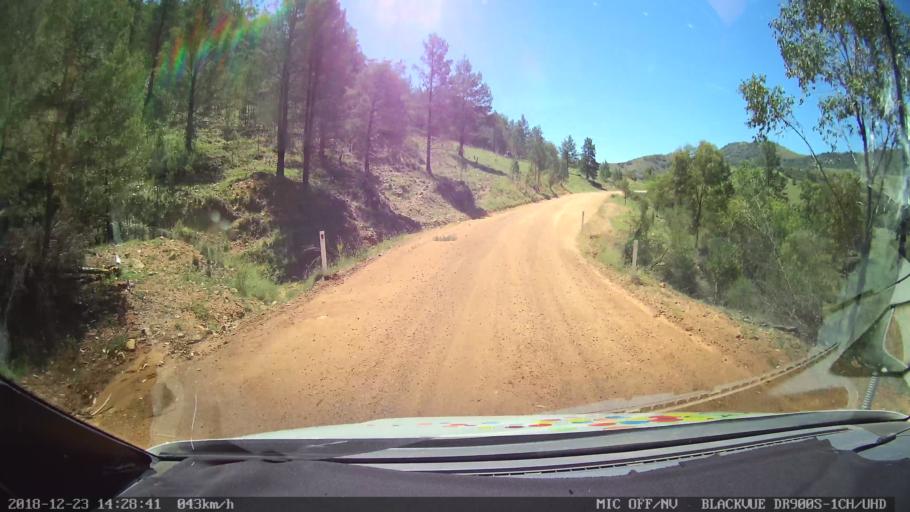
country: AU
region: New South Wales
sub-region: Tamworth Municipality
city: Manilla
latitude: -30.6131
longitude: 150.9405
